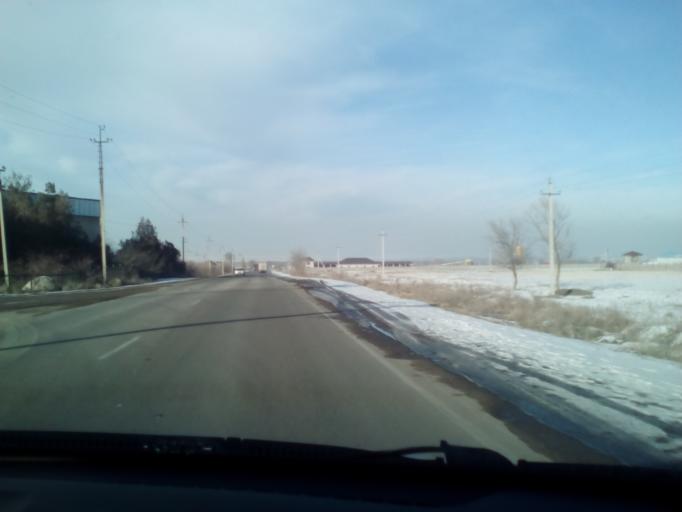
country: KZ
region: Almaty Oblysy
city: Burunday
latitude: 43.1989
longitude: 76.4149
